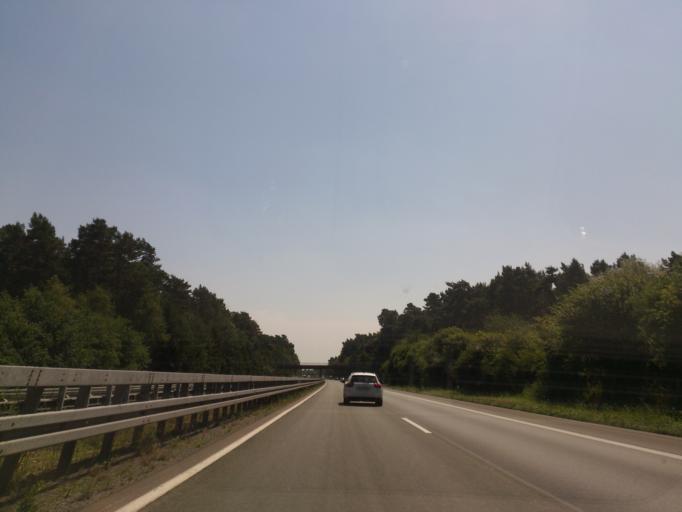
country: DE
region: North Rhine-Westphalia
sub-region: Regierungsbezirk Detmold
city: Oerlinghausen
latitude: 51.8895
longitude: 8.6416
